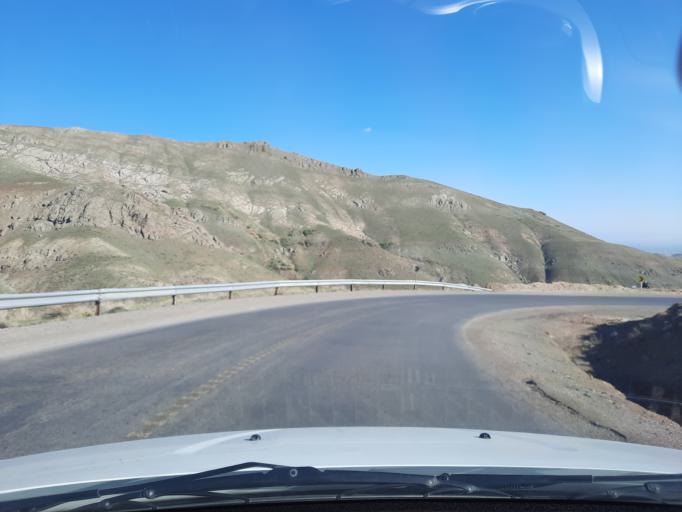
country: IR
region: Qazvin
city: Qazvin
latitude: 36.3690
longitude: 50.2046
